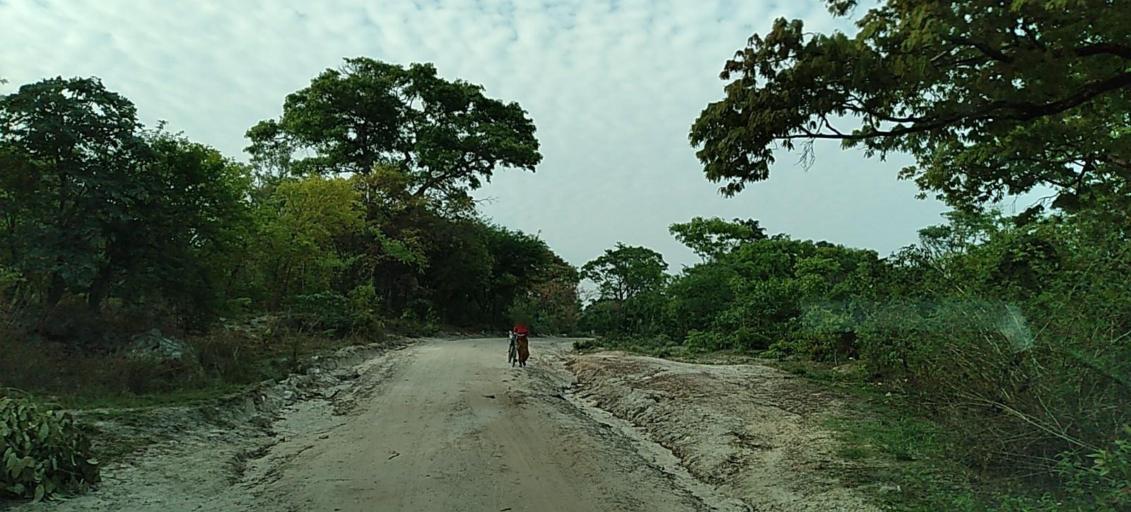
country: ZM
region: Copperbelt
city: Kalulushi
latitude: -12.8937
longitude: 27.6883
